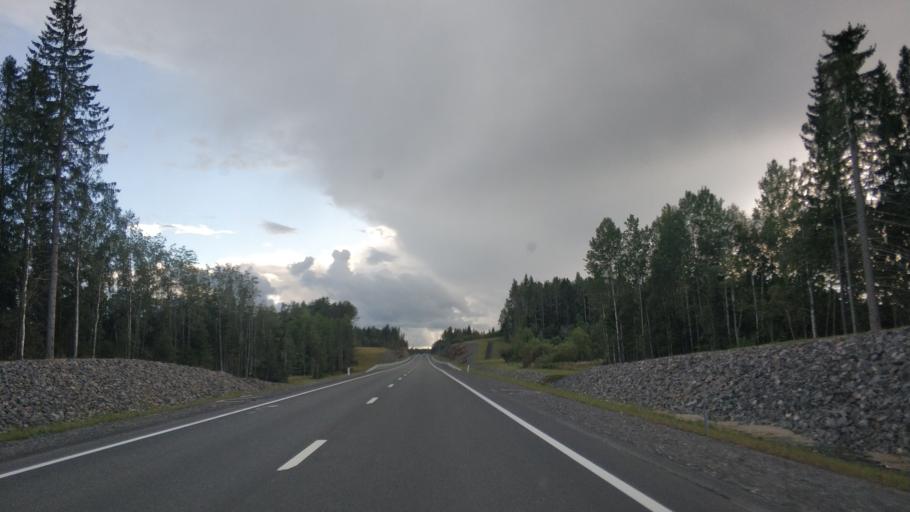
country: RU
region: Republic of Karelia
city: Lakhdenpokh'ya
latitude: 61.4397
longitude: 29.9832
